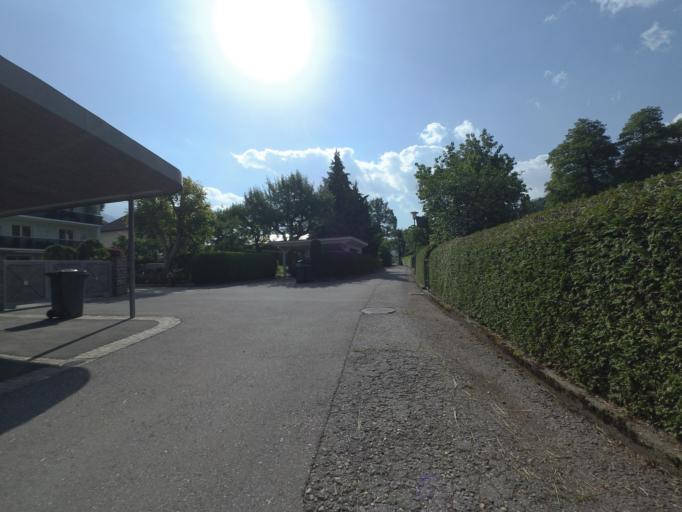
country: AT
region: Carinthia
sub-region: Politischer Bezirk Spittal an der Drau
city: Seeboden
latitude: 46.8146
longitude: 13.5071
